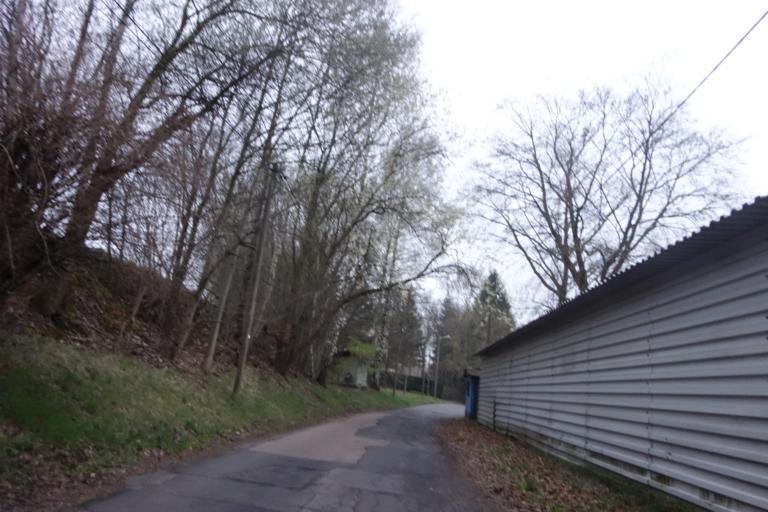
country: DE
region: Saxony
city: Freiberg
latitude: 50.9034
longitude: 13.3606
